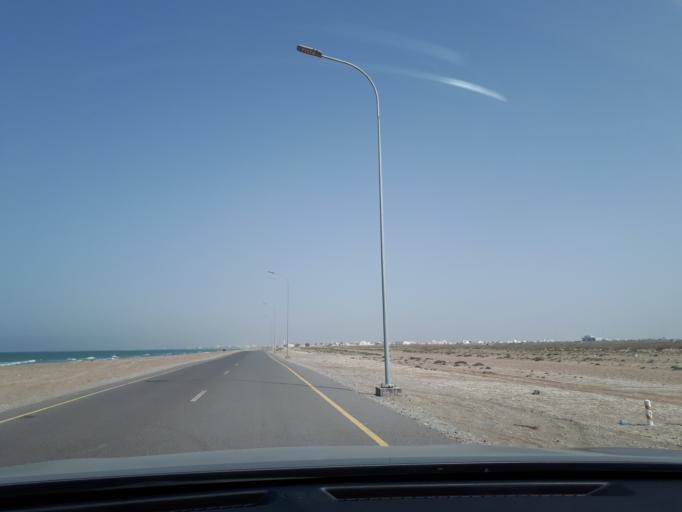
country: OM
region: Al Batinah
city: Barka'
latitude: 23.7275
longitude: 57.8419
